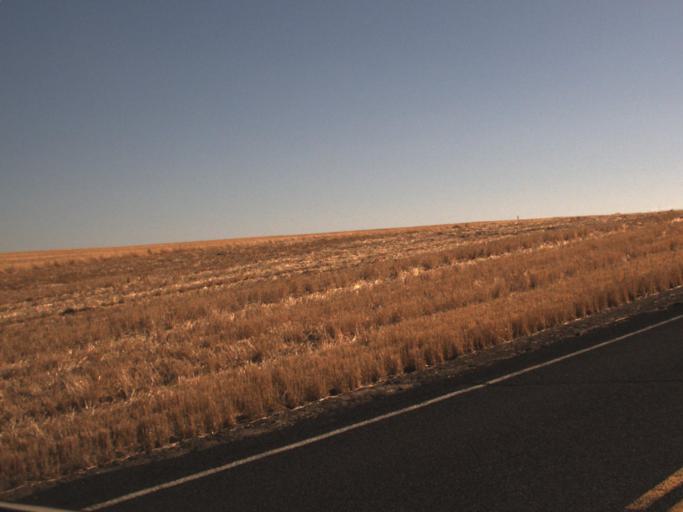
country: US
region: Washington
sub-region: Adams County
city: Ritzville
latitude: 46.9153
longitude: -118.5673
